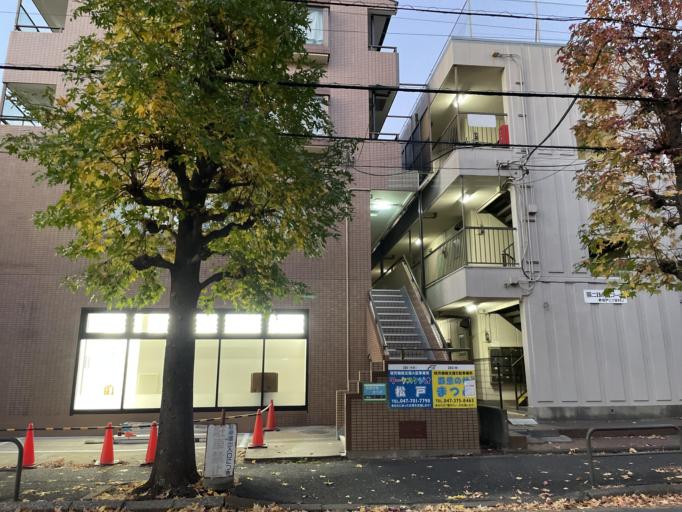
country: JP
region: Chiba
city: Nagareyama
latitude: 35.8246
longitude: 139.9140
